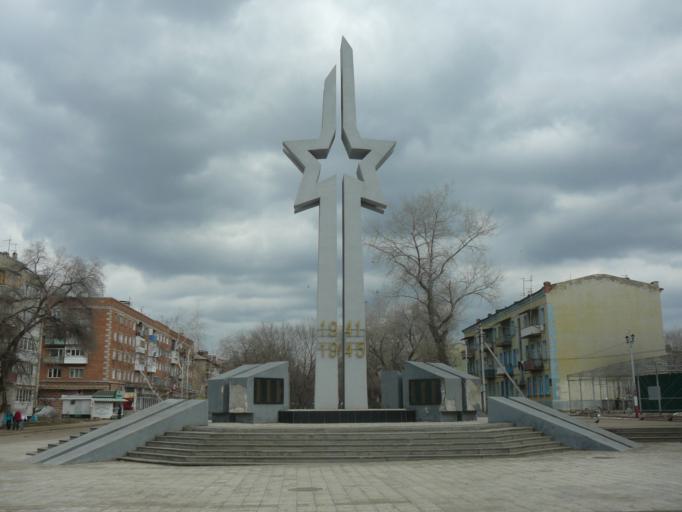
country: RU
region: Saratov
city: Privolzhskiy
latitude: 51.4124
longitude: 46.0465
